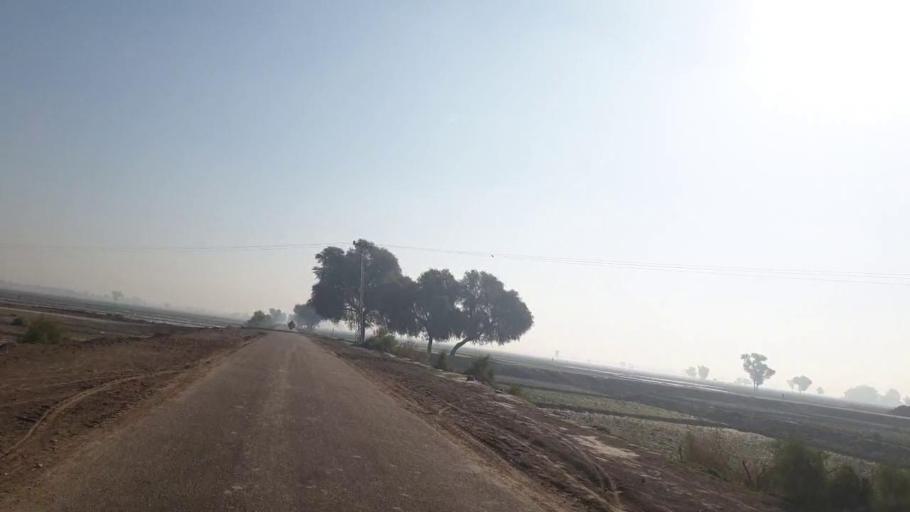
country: PK
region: Sindh
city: Dadu
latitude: 26.6723
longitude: 67.8263
